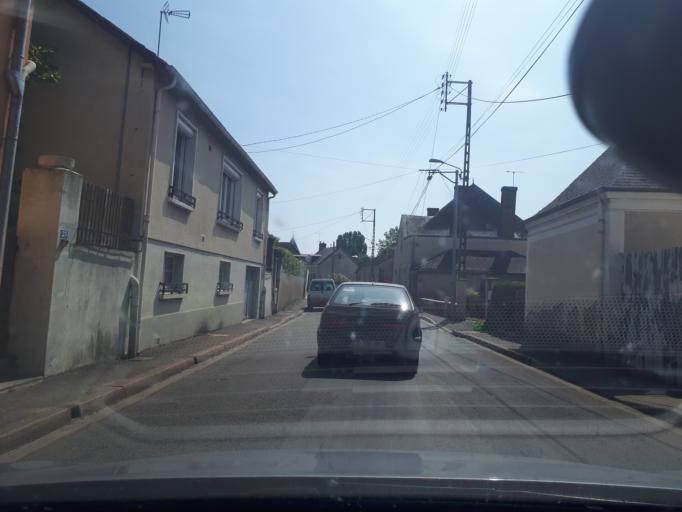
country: FR
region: Pays de la Loire
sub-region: Departement de la Sarthe
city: Montfort-le-Gesnois
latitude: 48.0481
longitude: 0.4019
